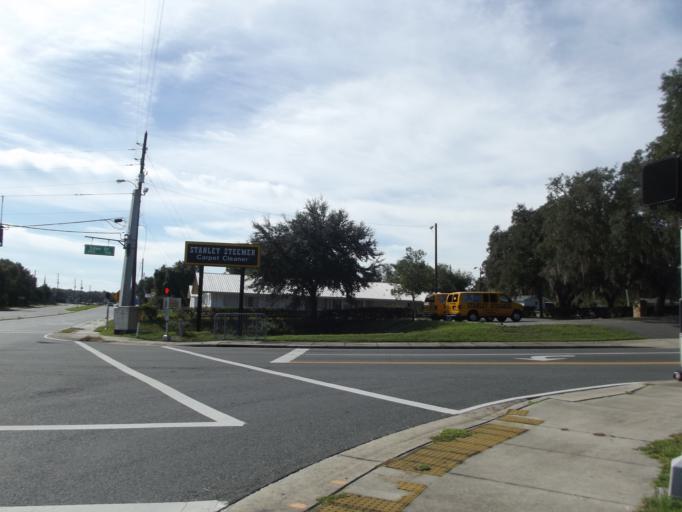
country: US
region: Florida
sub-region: Citrus County
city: Inverness
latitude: 28.8232
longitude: -82.3186
